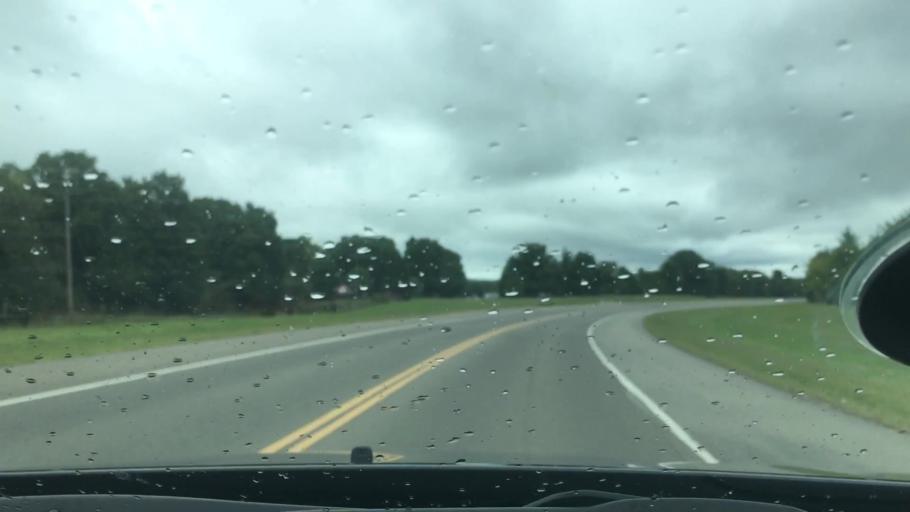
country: US
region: Oklahoma
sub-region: Sequoyah County
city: Vian
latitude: 35.5738
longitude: -94.9852
